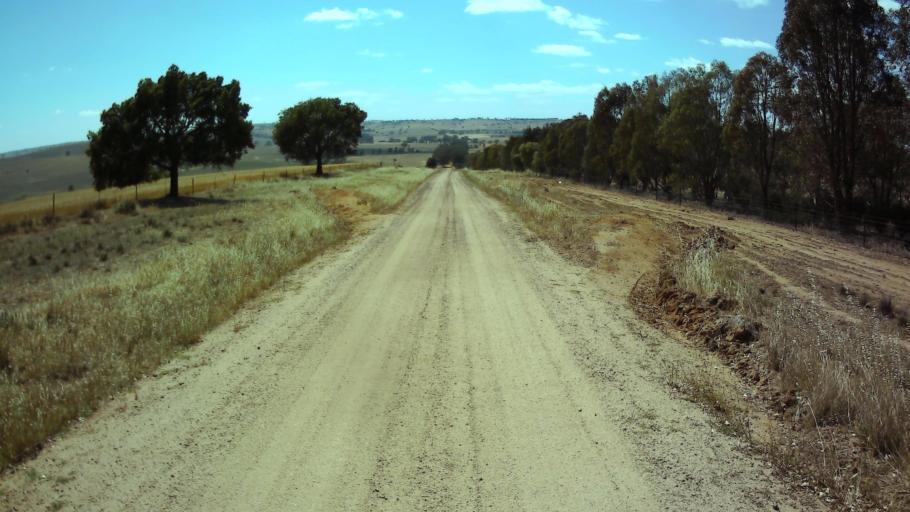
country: AU
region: New South Wales
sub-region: Weddin
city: Grenfell
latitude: -33.9534
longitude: 148.4017
